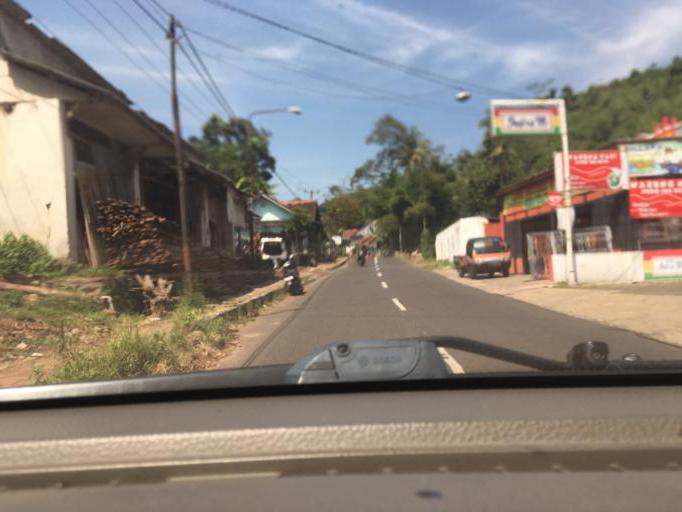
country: ID
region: West Java
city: Cilengkrang
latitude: -6.9550
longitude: 108.0951
